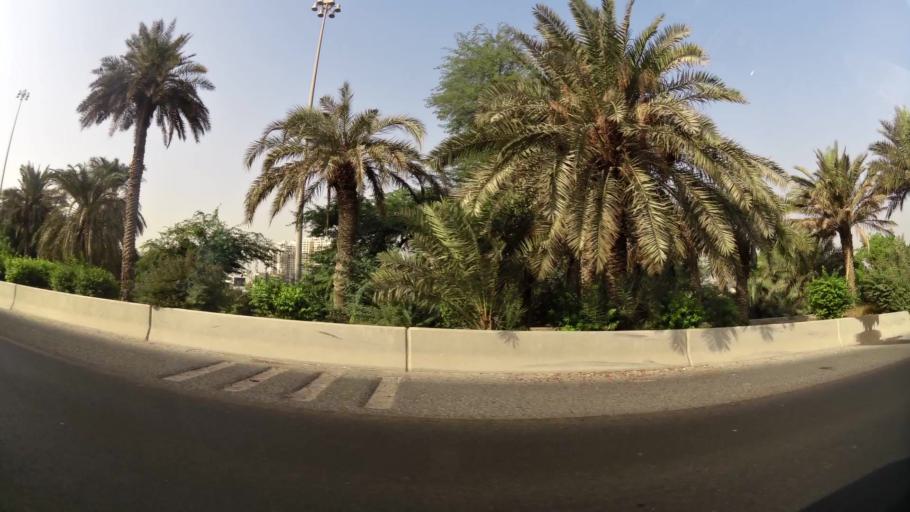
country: KW
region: Muhafazat Hawalli
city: Salwa
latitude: 29.2696
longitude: 48.0844
